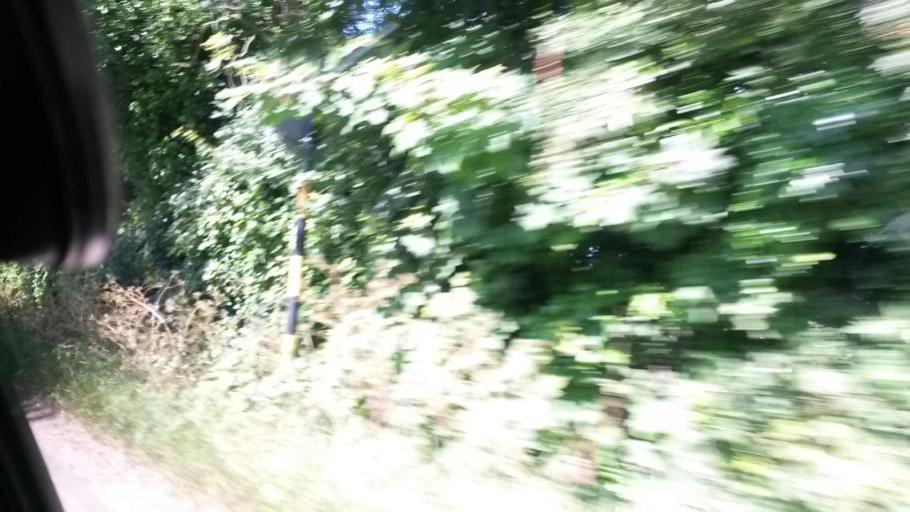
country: IE
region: Leinster
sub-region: An Mhi
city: Stamullin
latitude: 53.5790
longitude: -6.2843
